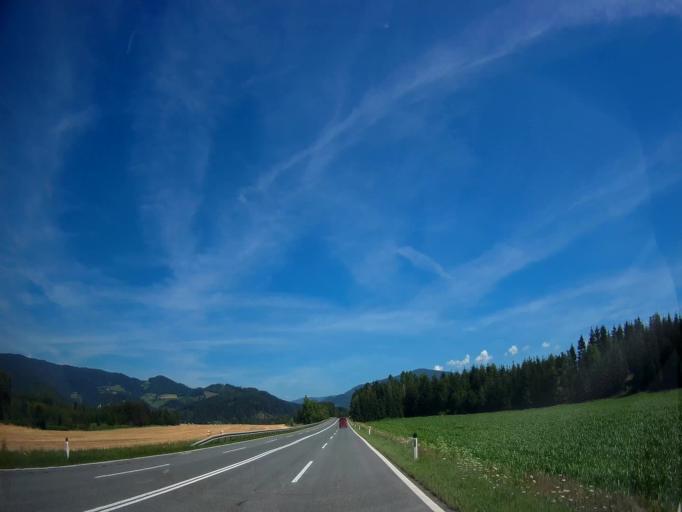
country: AT
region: Carinthia
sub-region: Politischer Bezirk Sankt Veit an der Glan
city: Molbling
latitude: 46.8492
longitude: 14.4482
